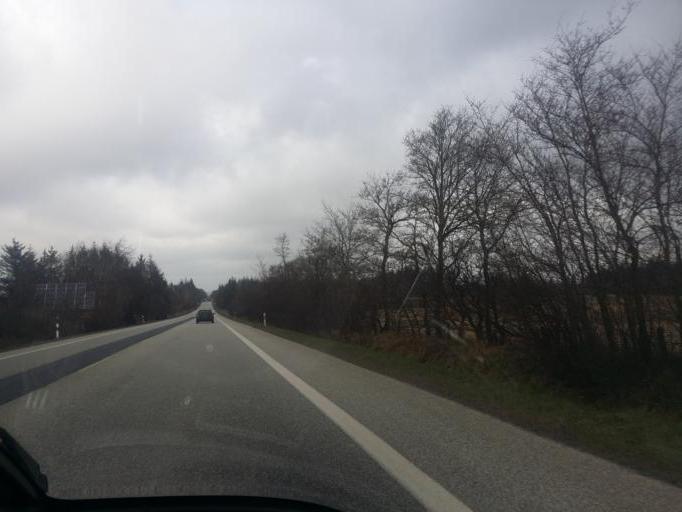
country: DE
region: Schleswig-Holstein
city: Bordelum
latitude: 54.6489
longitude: 8.9468
